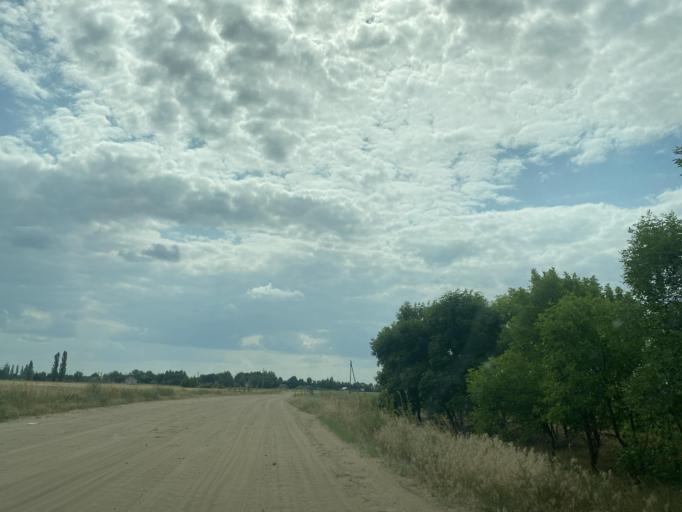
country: BY
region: Brest
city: Ivanava
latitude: 52.3575
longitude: 25.6319
